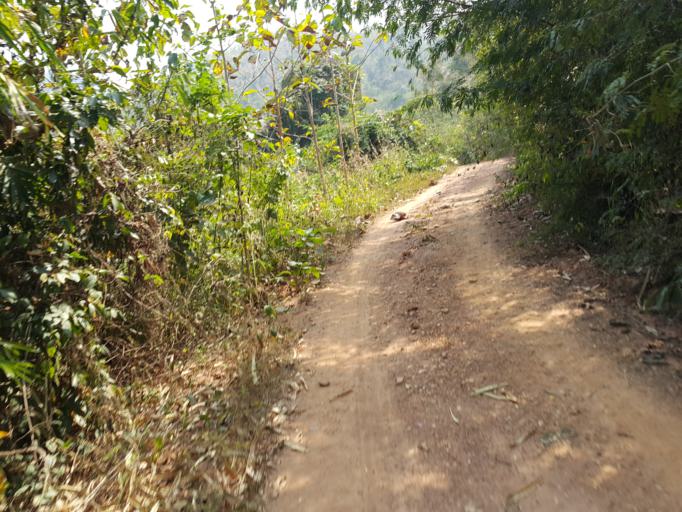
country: TH
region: Sukhothai
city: Thung Saliam
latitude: 17.3255
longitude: 99.4993
